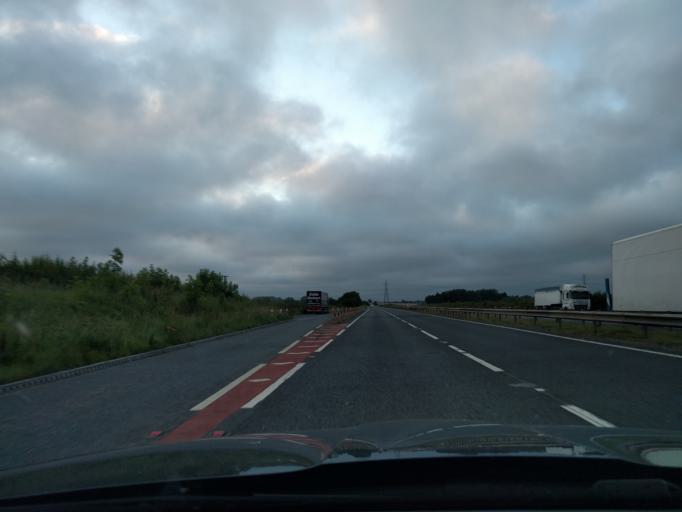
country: GB
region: England
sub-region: Northumberland
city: Stannington
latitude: 55.1216
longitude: -1.6722
